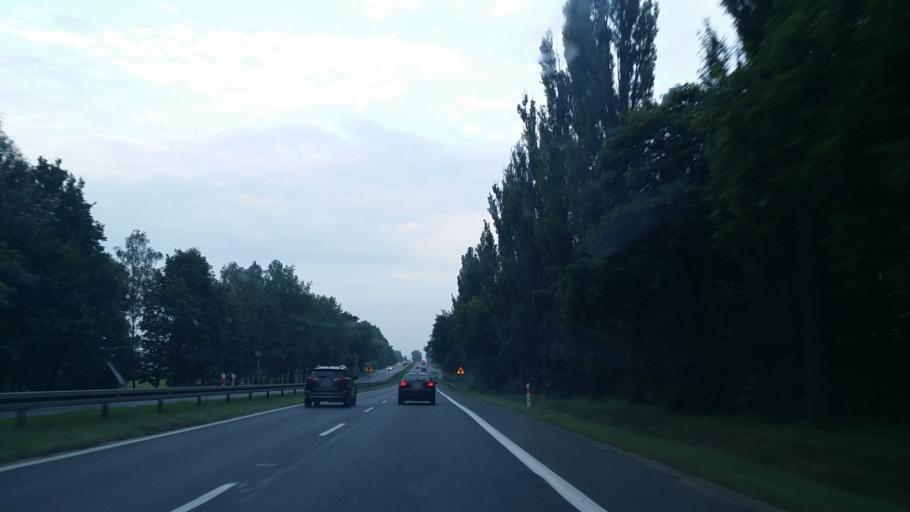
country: PL
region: Lower Silesian Voivodeship
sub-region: Powiat lubinski
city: Lubin
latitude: 51.4262
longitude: 16.1754
